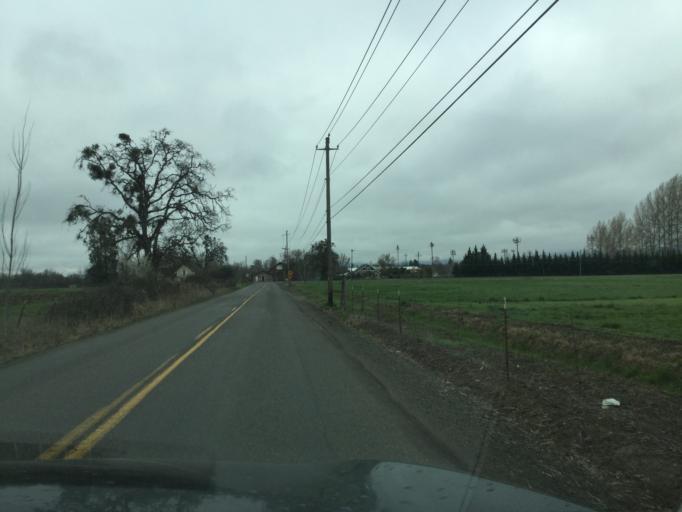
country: US
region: Oregon
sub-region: Jackson County
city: Central Point
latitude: 42.3948
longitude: -122.9093
